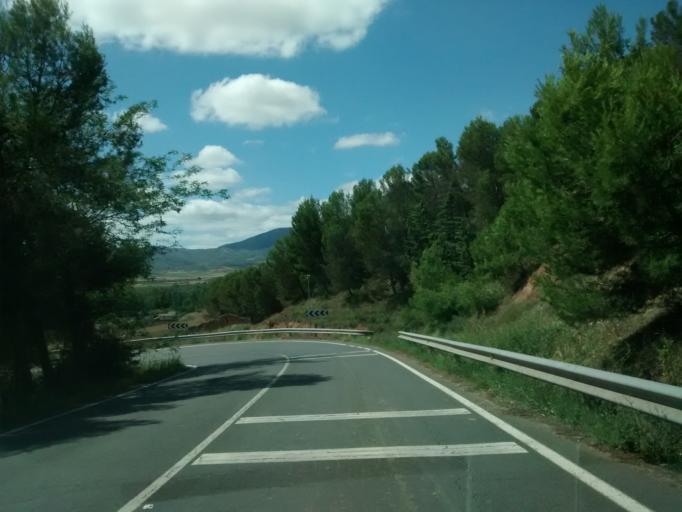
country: ES
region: La Rioja
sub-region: Provincia de La Rioja
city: Murillo de Rio Leza
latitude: 42.3979
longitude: -2.3353
